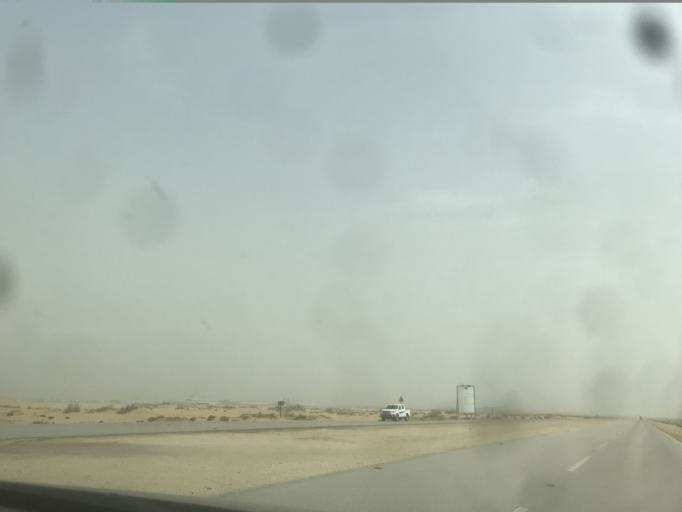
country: SA
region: Eastern Province
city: Abqaiq
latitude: 25.9085
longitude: 49.9277
